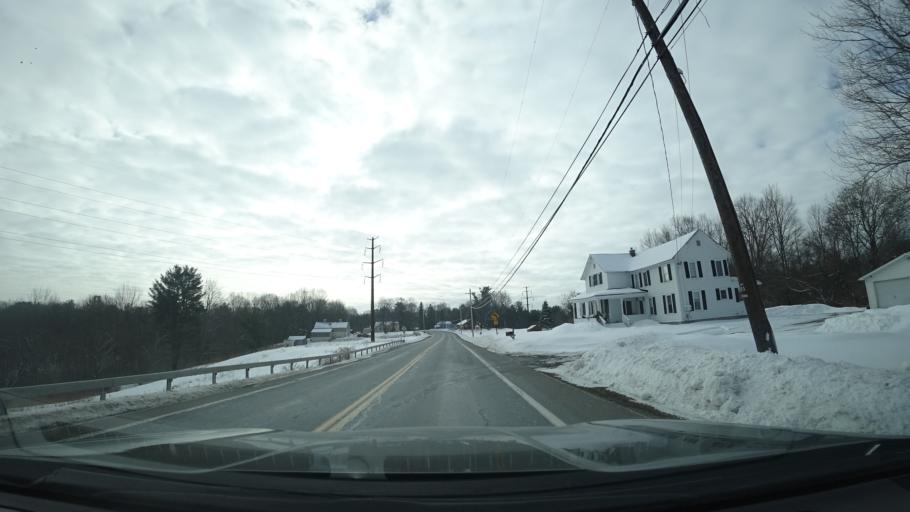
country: US
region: New York
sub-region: Washington County
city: Fort Edward
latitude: 43.2641
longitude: -73.6084
